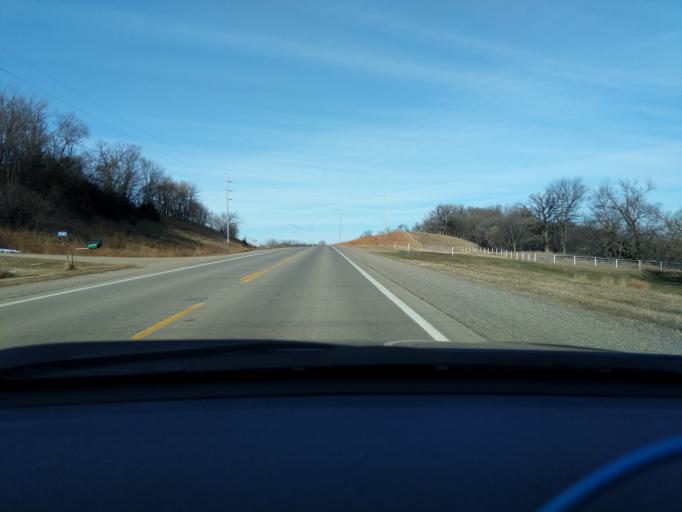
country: US
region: Minnesota
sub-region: Yellow Medicine County
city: Granite Falls
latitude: 44.7940
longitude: -95.4556
